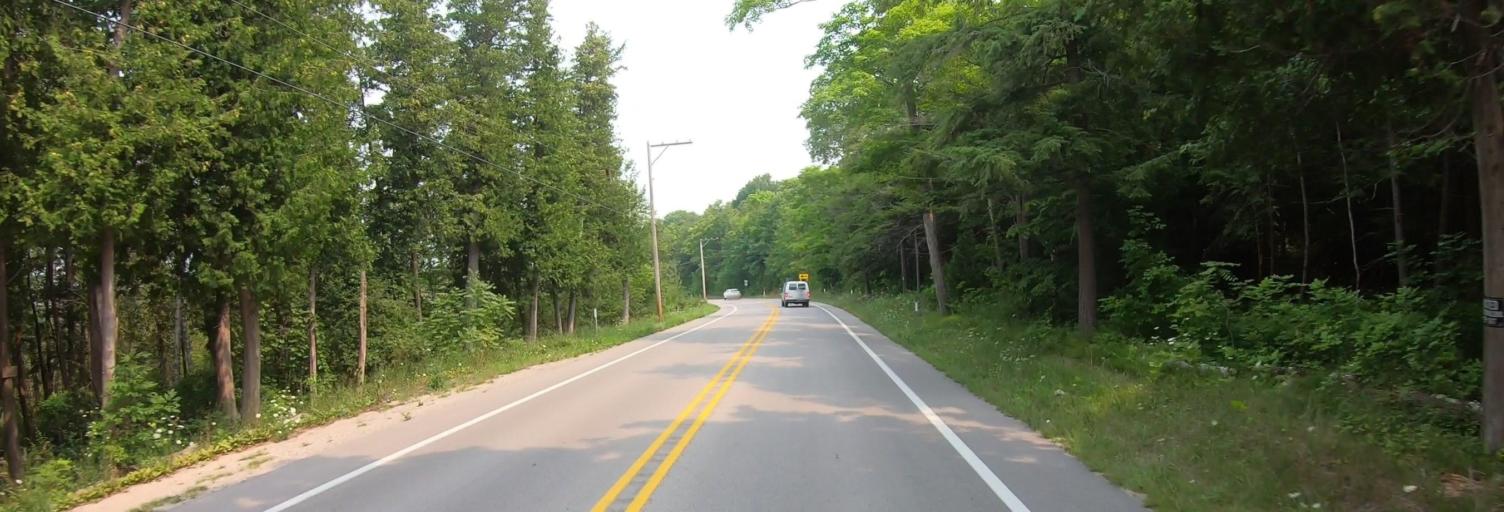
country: US
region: Michigan
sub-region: Leelanau County
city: Leland
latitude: 44.9901
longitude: -85.7712
